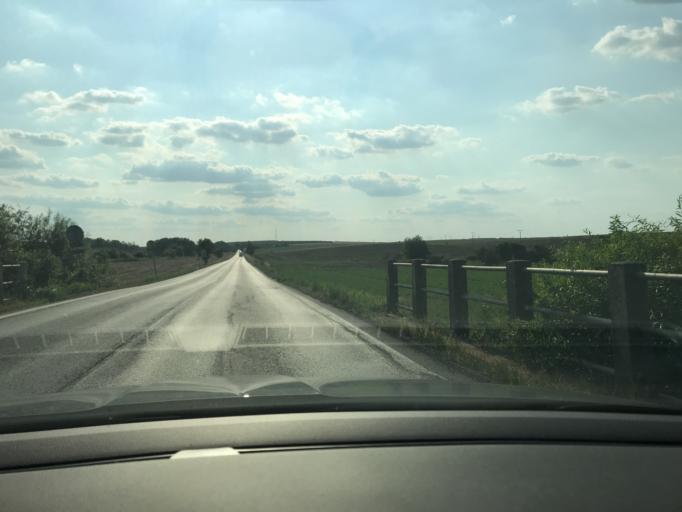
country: CZ
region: Central Bohemia
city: Velvary
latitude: 50.2635
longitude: 14.1894
